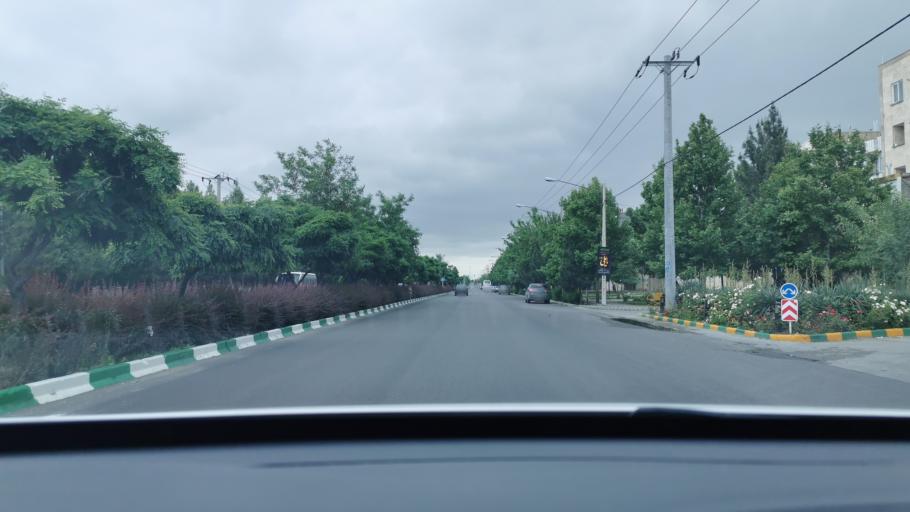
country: IR
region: Razavi Khorasan
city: Mashhad
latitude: 36.3710
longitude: 59.5068
